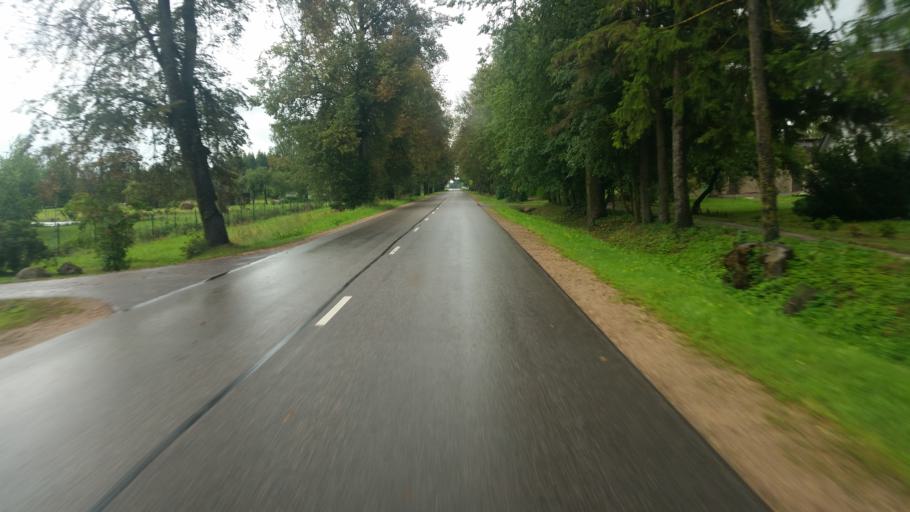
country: LV
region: Bauskas Rajons
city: Bauska
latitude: 56.4323
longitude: 24.3455
